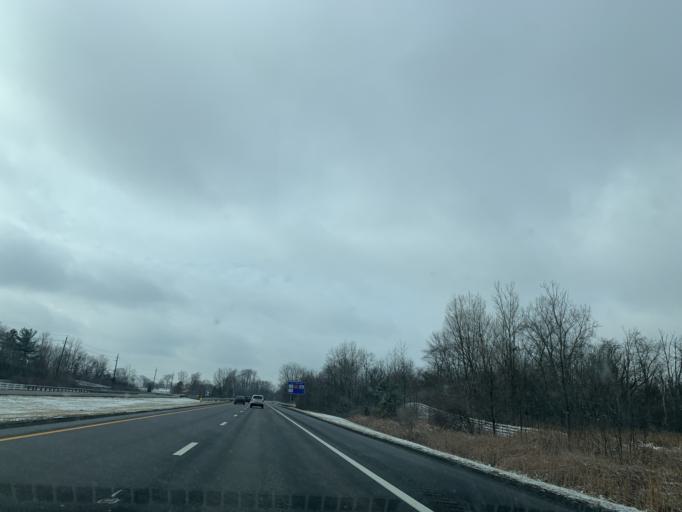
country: US
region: Ohio
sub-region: Franklin County
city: New Albany
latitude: 40.0804
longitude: -82.7822
